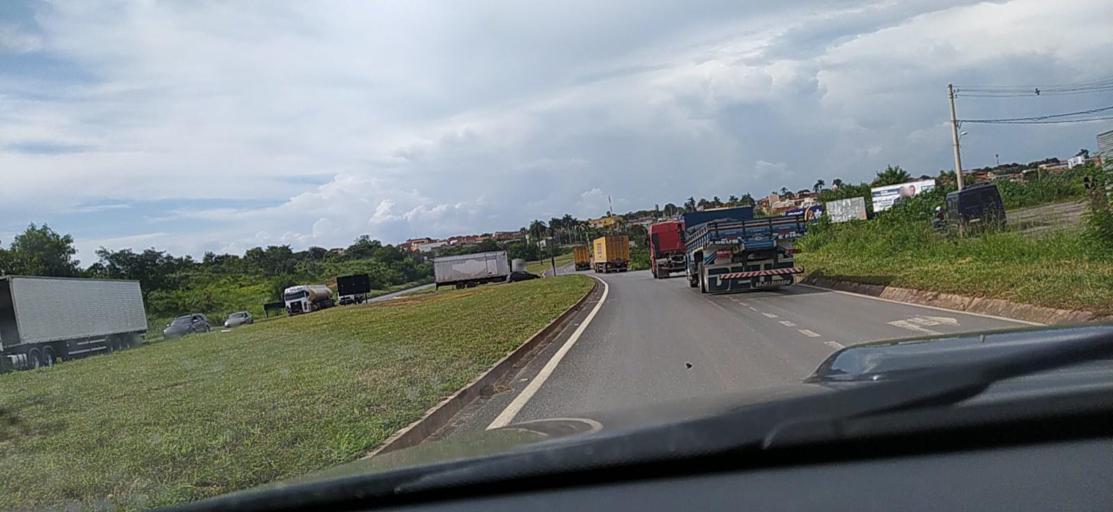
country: BR
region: Minas Gerais
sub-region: Montes Claros
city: Montes Claros
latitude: -16.7530
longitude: -43.8456
